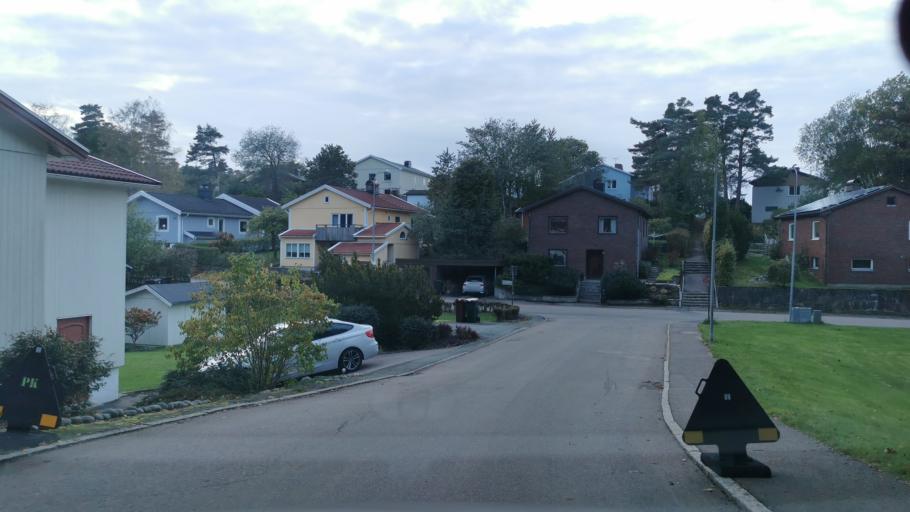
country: SE
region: Vaestra Goetaland
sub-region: Partille Kommun
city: Partille
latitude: 57.7210
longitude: 12.0939
